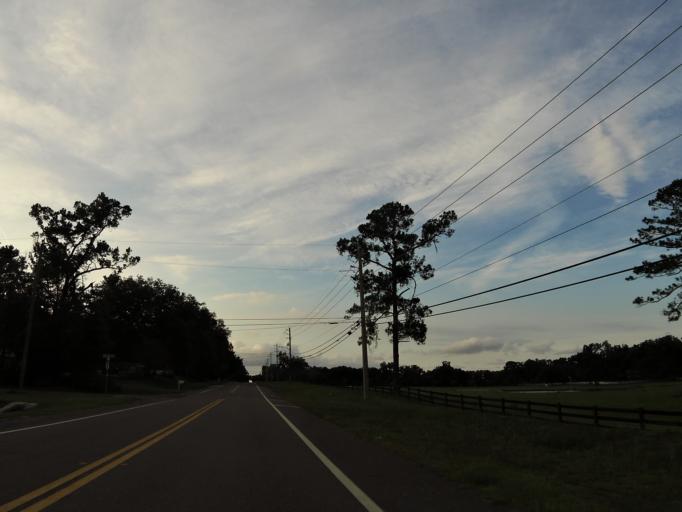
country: US
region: Florida
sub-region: Duval County
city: Jacksonville
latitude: 30.3500
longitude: -81.8069
